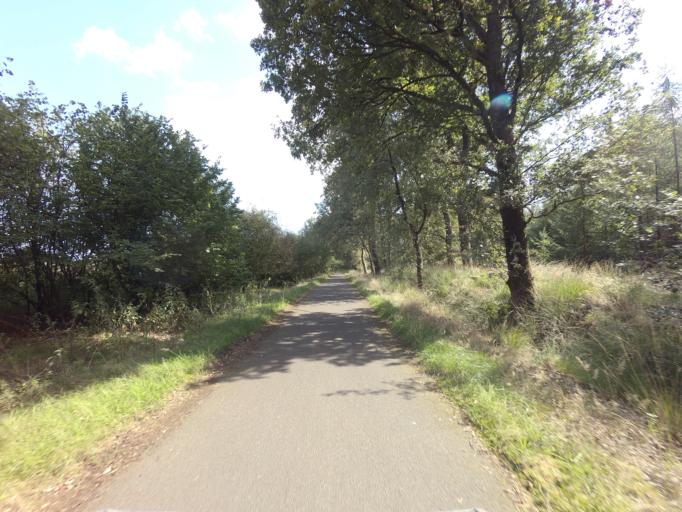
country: NL
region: Drenthe
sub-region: Gemeente Westerveld
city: Dwingeloo
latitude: 52.8324
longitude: 6.4724
